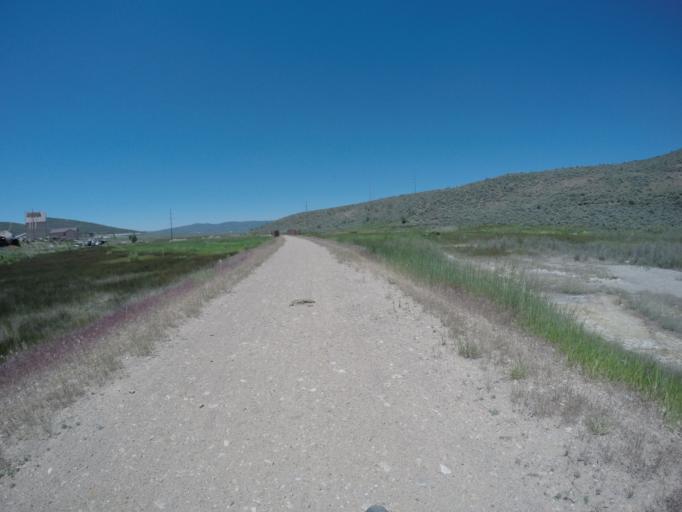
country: US
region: Utah
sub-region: Summit County
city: Park City
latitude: 40.6885
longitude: -111.4574
